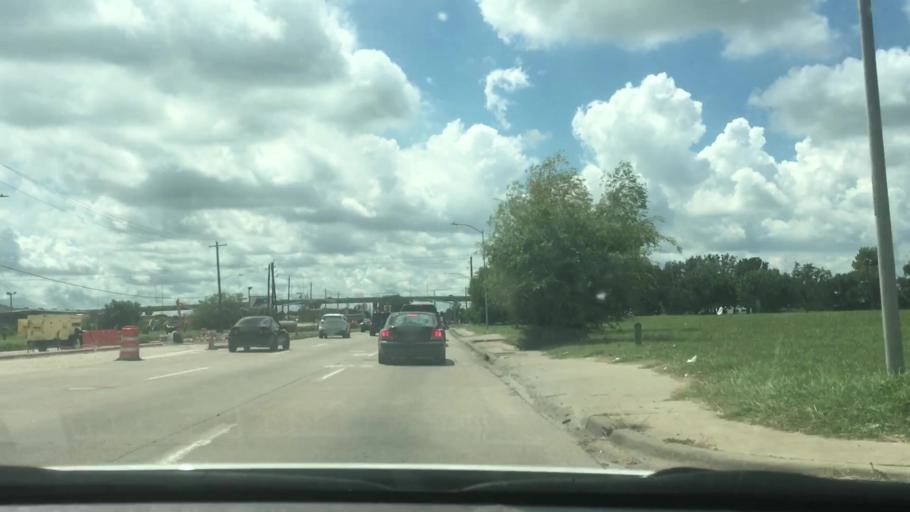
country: US
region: Texas
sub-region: Harris County
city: Bellaire
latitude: 29.6528
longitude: -95.4640
